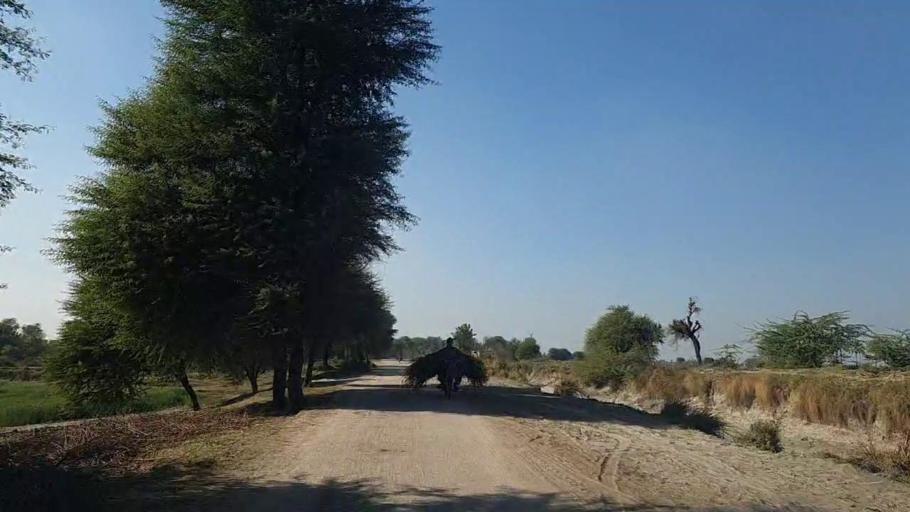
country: PK
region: Sindh
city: Shahpur Chakar
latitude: 26.2137
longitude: 68.6102
